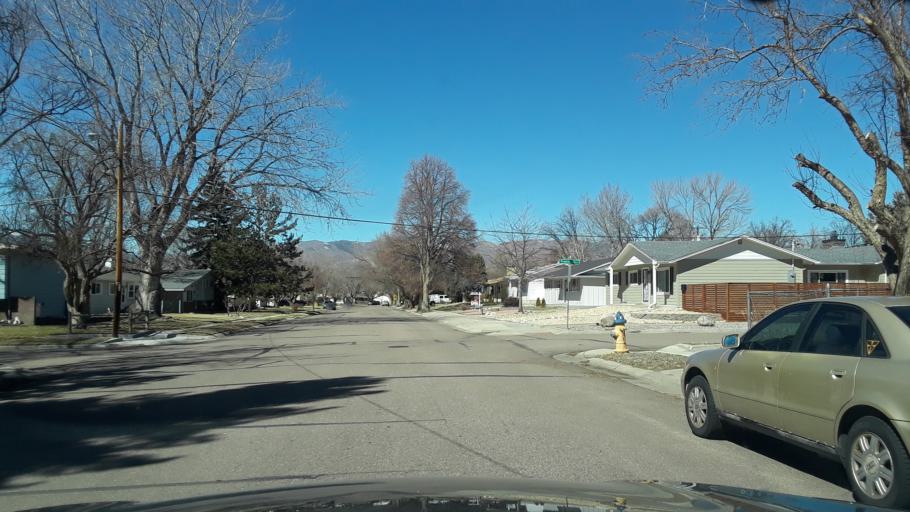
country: US
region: Colorado
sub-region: El Paso County
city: Colorado Springs
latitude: 38.8688
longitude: -104.8067
